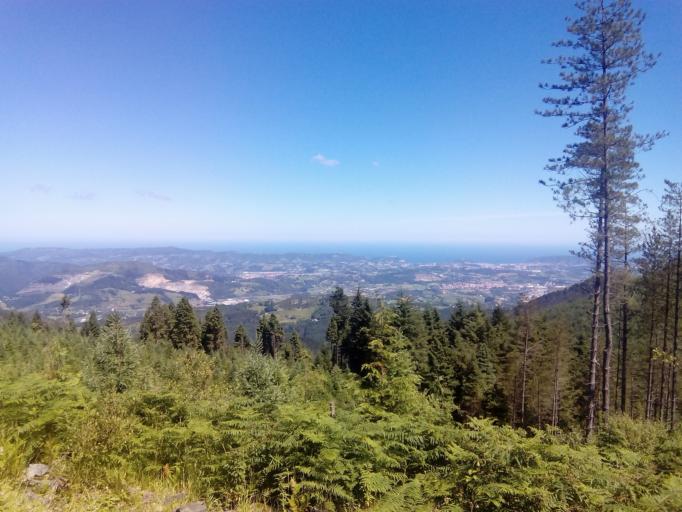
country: ES
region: Basque Country
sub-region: Provincia de Guipuzcoa
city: Urnieta
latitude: 43.1982
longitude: -1.9694
